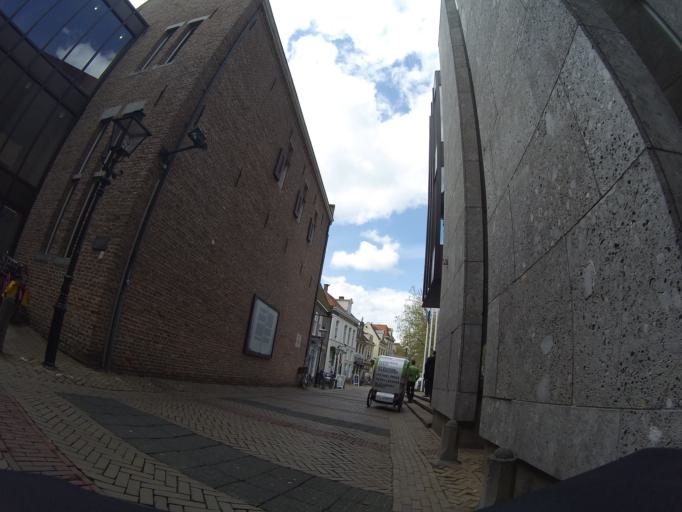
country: NL
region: Overijssel
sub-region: Gemeente Zwolle
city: Zwolle
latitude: 52.5111
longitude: 6.0930
